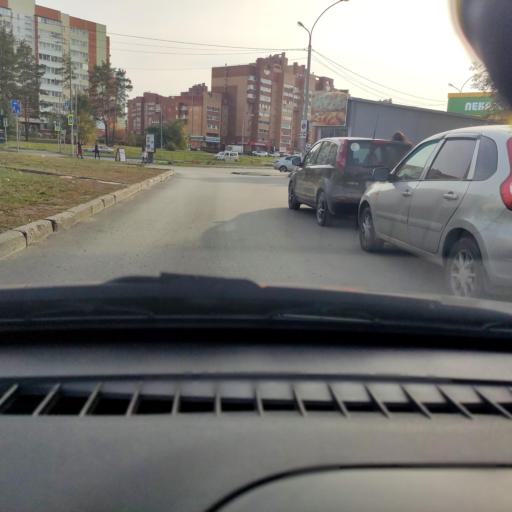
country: RU
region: Samara
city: Tol'yatti
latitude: 53.5391
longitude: 49.3575
